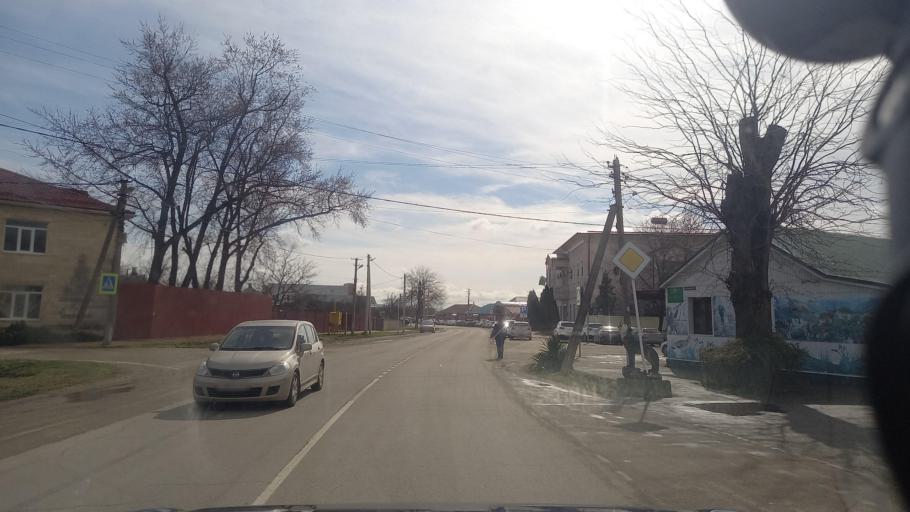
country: RU
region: Adygeya
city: Takhtamukay
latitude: 44.9235
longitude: 38.9930
